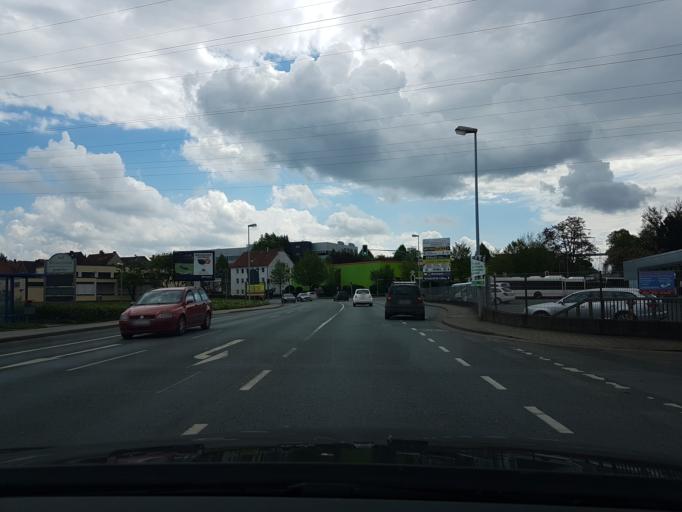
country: DE
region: Lower Saxony
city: Hameln
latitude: 52.1007
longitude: 9.3916
